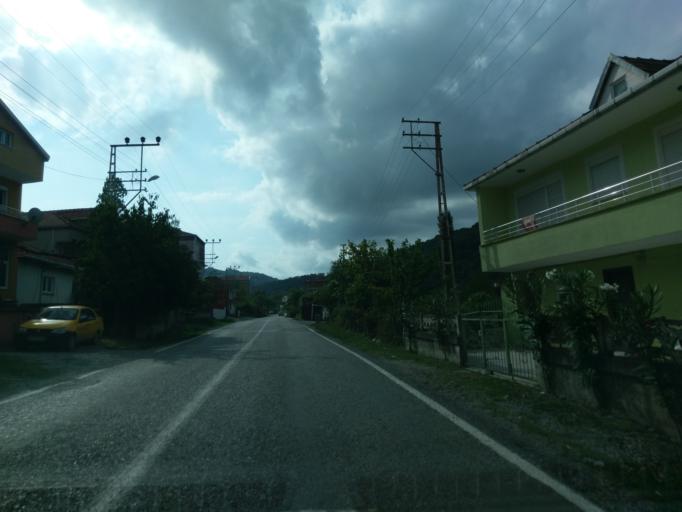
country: TR
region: Sinop
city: Helaldi
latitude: 41.9390
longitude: 34.4034
